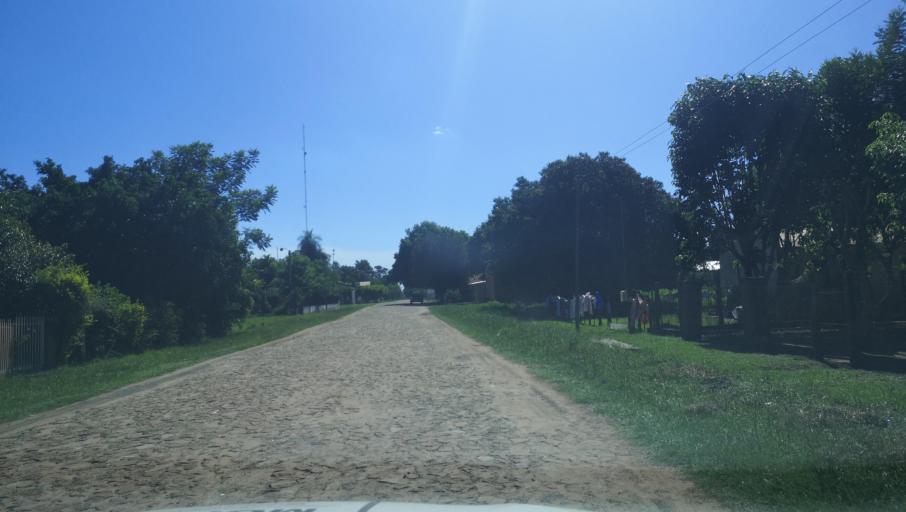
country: PY
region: Caaguazu
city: Carayao
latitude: -25.1953
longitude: -56.3984
